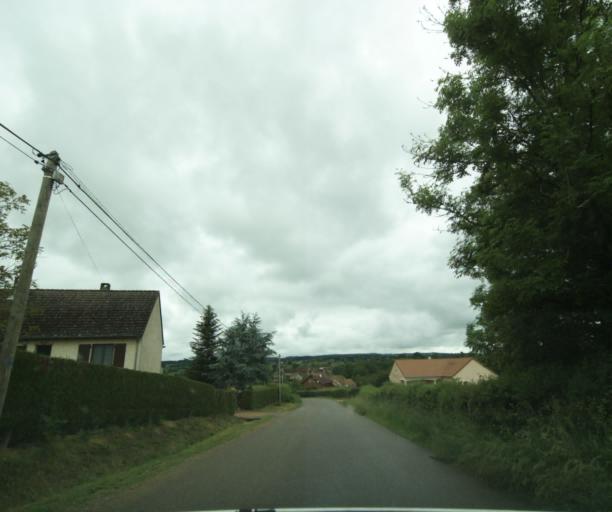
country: FR
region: Bourgogne
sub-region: Departement de Saone-et-Loire
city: Charolles
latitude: 46.4702
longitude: 4.3387
